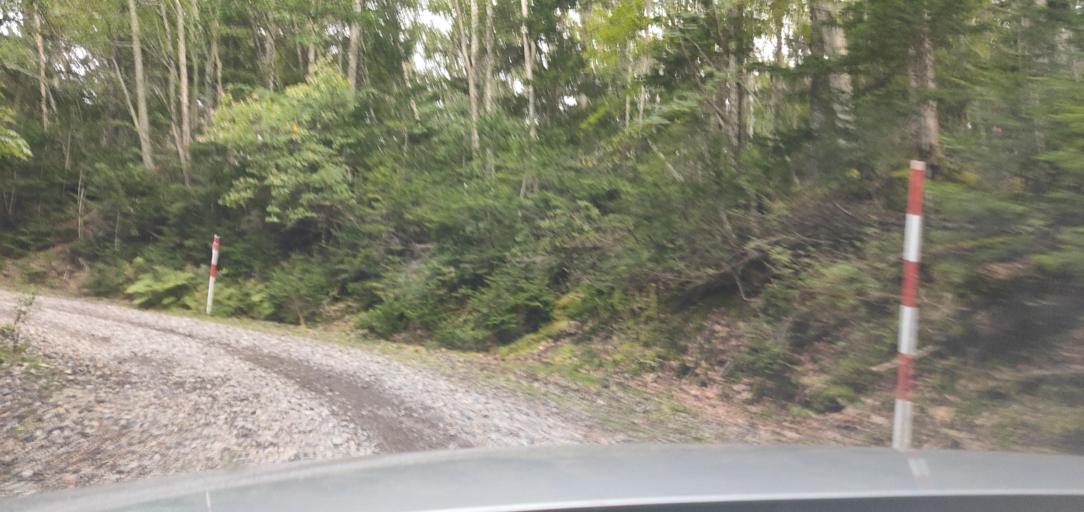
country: JP
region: Hokkaido
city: Kitami
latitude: 43.3691
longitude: 143.9493
